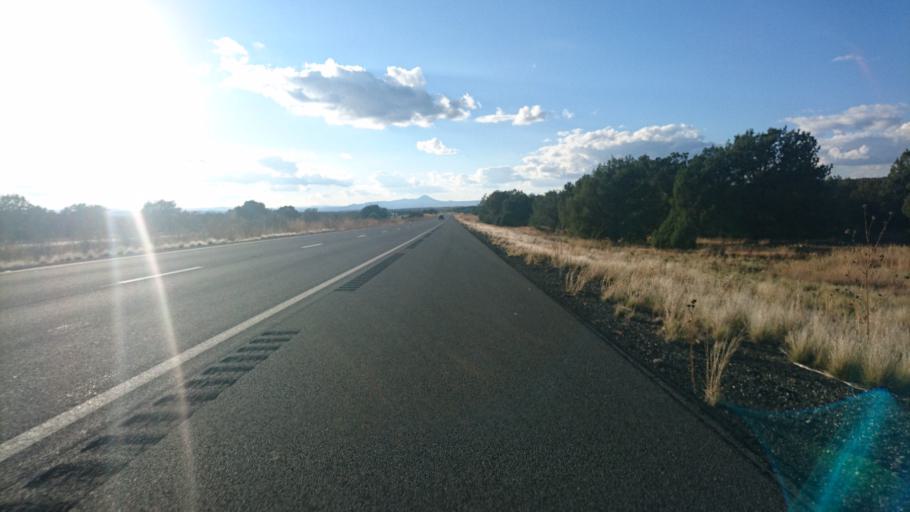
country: US
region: Arizona
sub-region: Coconino County
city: Williams
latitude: 35.2136
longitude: -112.4127
